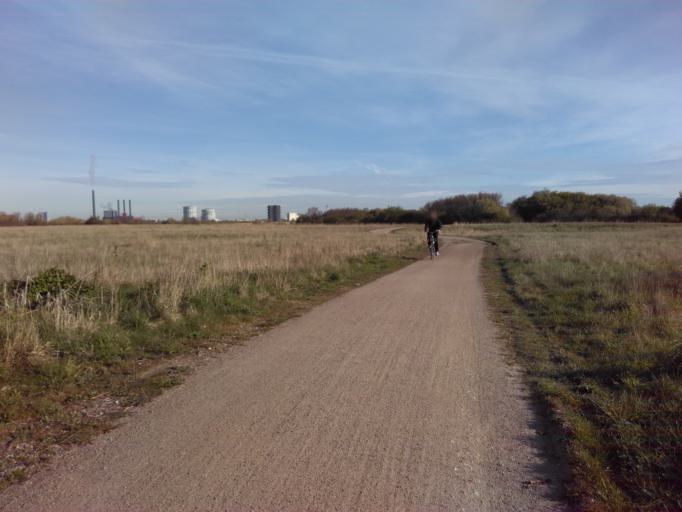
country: DK
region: Capital Region
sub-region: Tarnby Kommune
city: Tarnby
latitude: 55.6431
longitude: 12.5756
